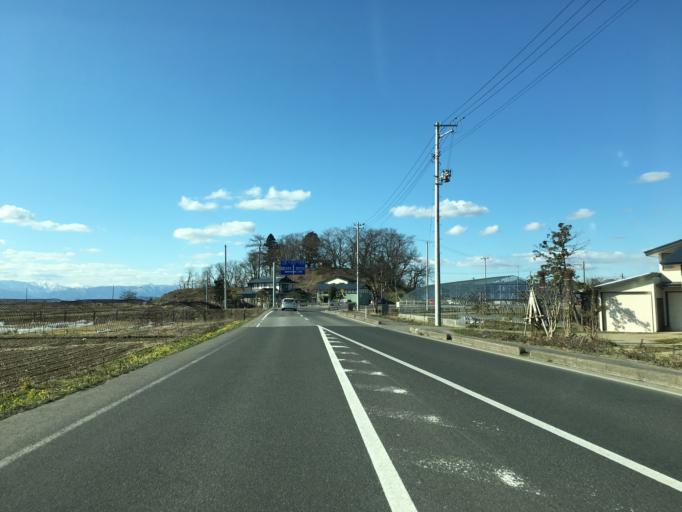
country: JP
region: Yamagata
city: Takahata
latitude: 37.9921
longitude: 140.1795
